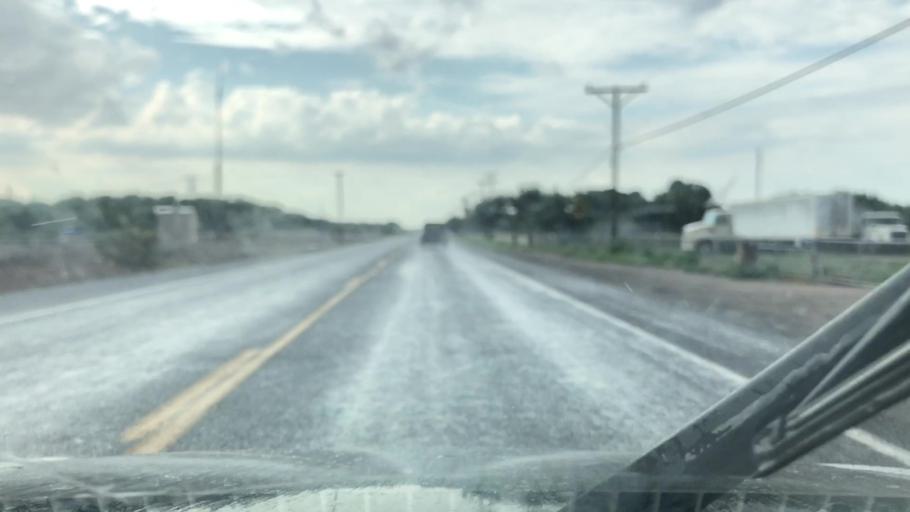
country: US
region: New Mexico
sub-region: Dona Ana County
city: Mesquite
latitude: 32.1912
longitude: -106.7133
